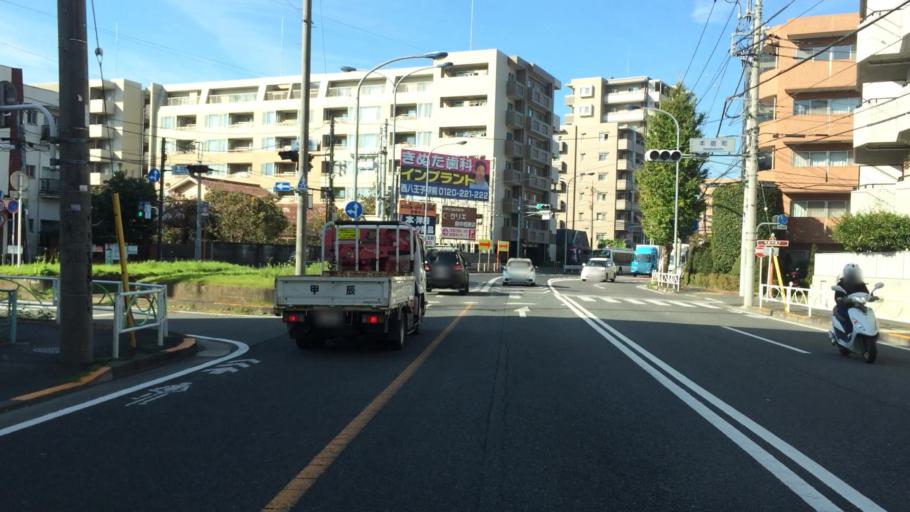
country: JP
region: Tokyo
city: Kokubunji
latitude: 35.6725
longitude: 139.4621
